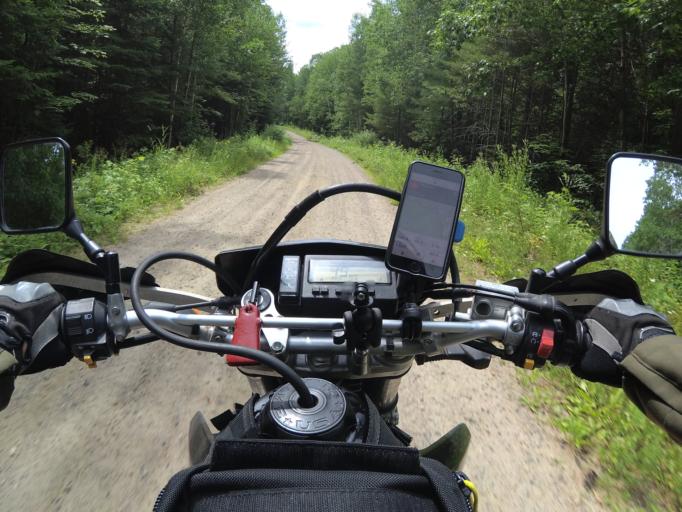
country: CA
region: Ontario
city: Bancroft
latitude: 44.8309
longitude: -77.2924
